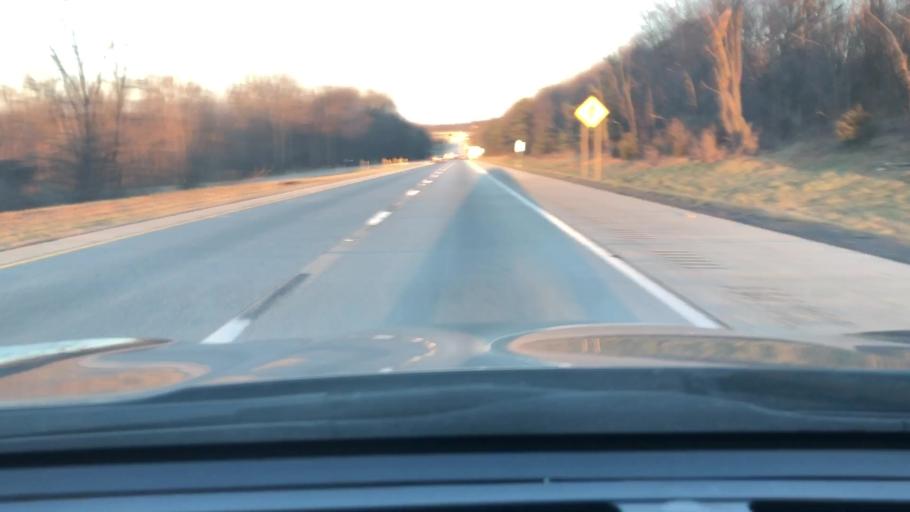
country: US
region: Pennsylvania
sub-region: Lebanon County
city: Jonestown
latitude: 40.4260
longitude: -76.5185
